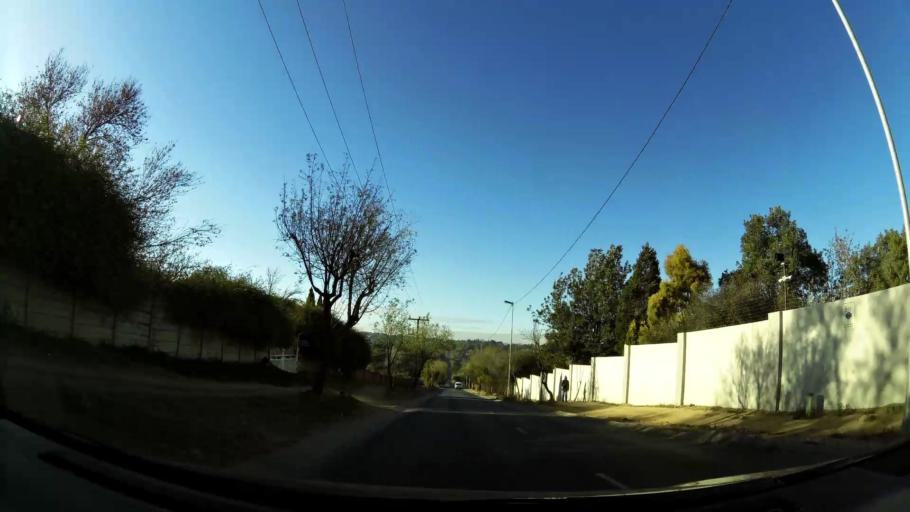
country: ZA
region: Gauteng
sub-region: City of Johannesburg Metropolitan Municipality
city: Midrand
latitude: -26.0158
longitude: 28.1387
